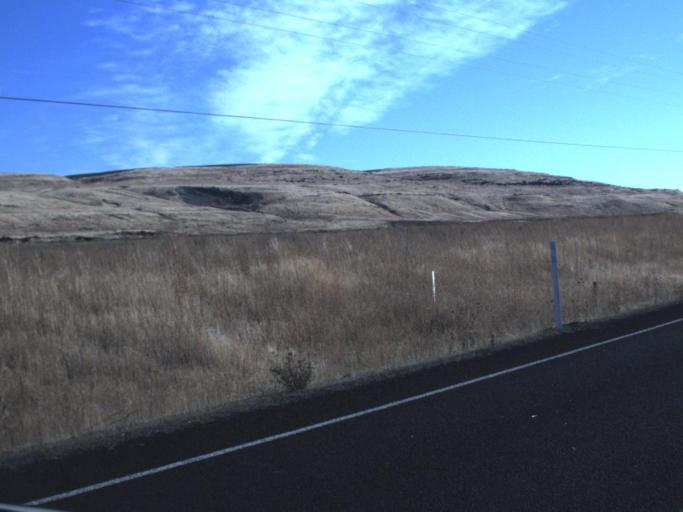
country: US
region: Washington
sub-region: Franklin County
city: Connell
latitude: 46.6494
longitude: -118.5967
